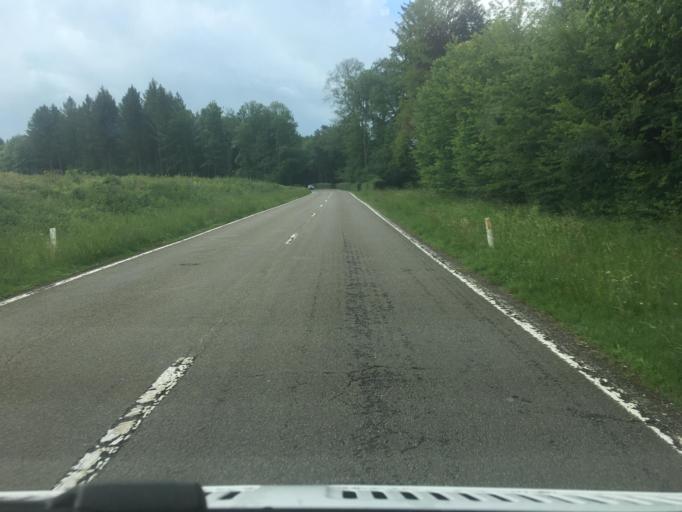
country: BE
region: Wallonia
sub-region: Province du Luxembourg
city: Florenville
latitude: 49.6502
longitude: 5.3385
